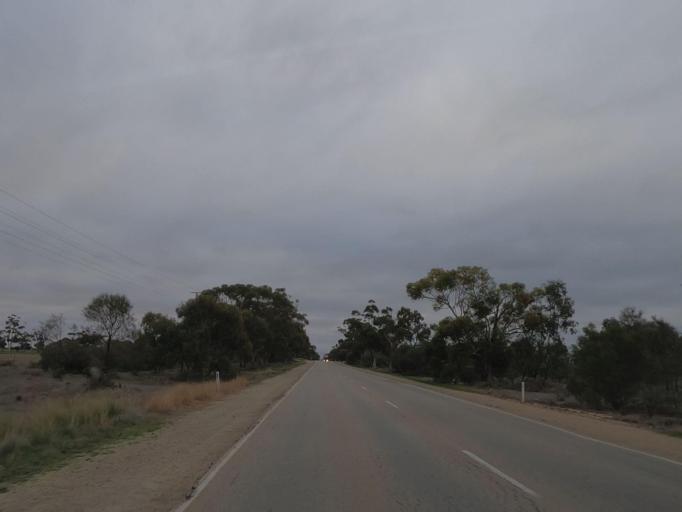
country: AU
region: Victoria
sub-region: Swan Hill
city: Swan Hill
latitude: -35.4083
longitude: 143.5833
